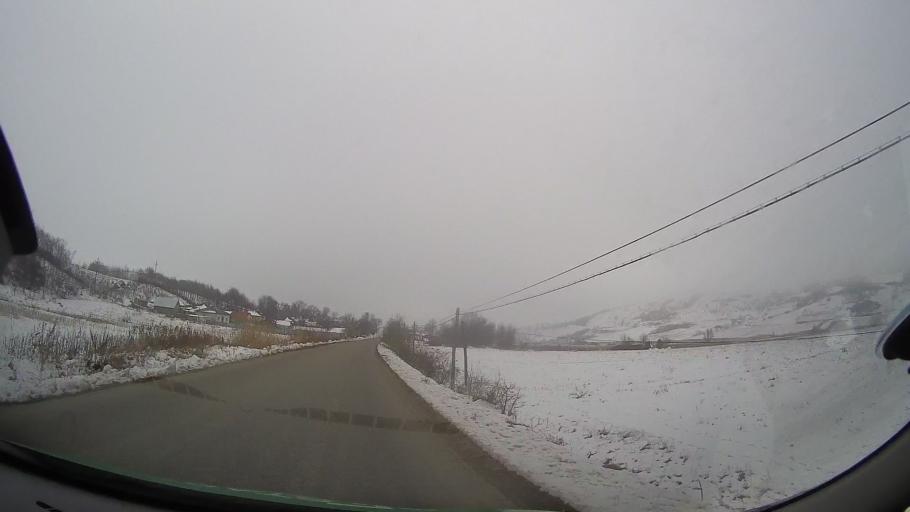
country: RO
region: Bacau
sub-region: Comuna Glavanesti
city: Frumuselu
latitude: 46.2914
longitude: 27.3010
